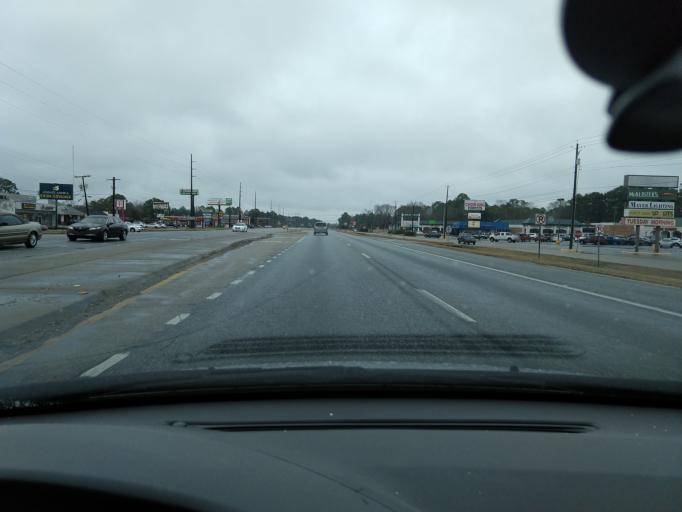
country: US
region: Alabama
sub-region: Houston County
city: Dothan
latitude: 31.2296
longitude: -85.4320
